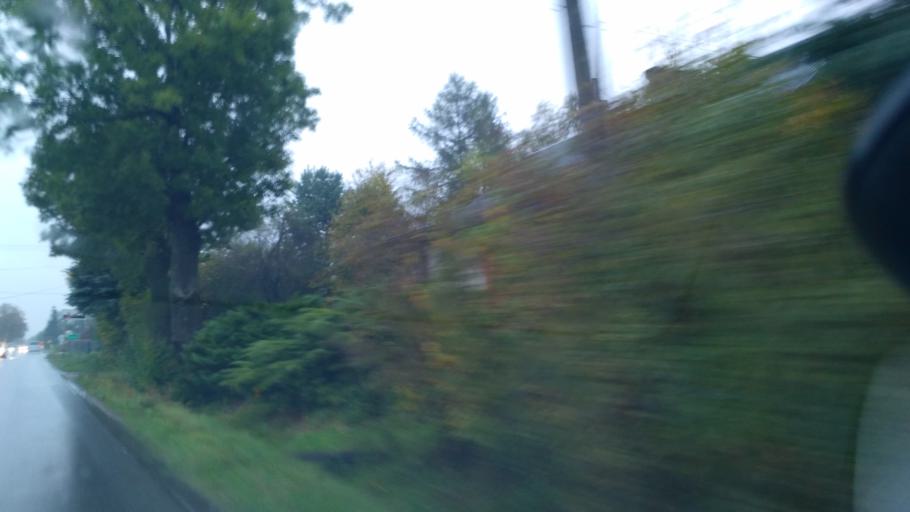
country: PL
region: Subcarpathian Voivodeship
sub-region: Powiat krosnienski
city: Miejsce Piastowe
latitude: 49.6591
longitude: 21.8032
